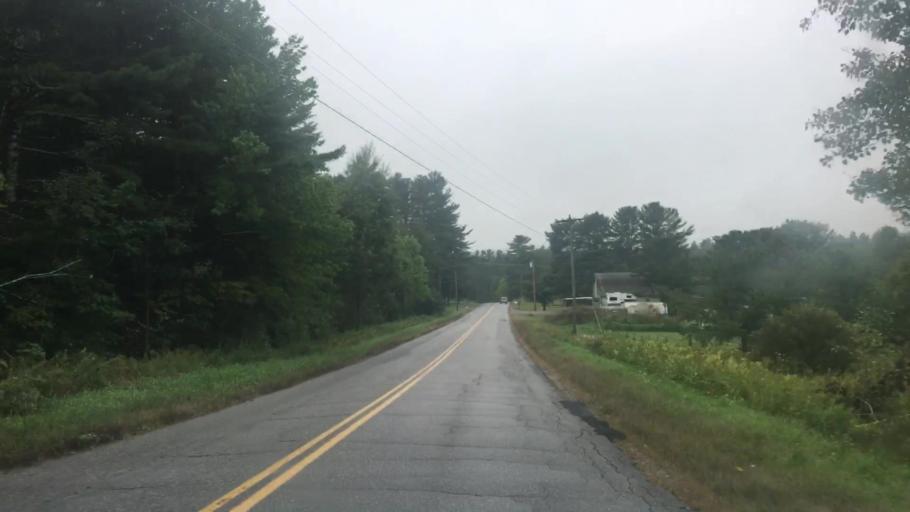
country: US
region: Maine
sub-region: Waldo County
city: Frankfort
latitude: 44.5517
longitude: -68.8680
